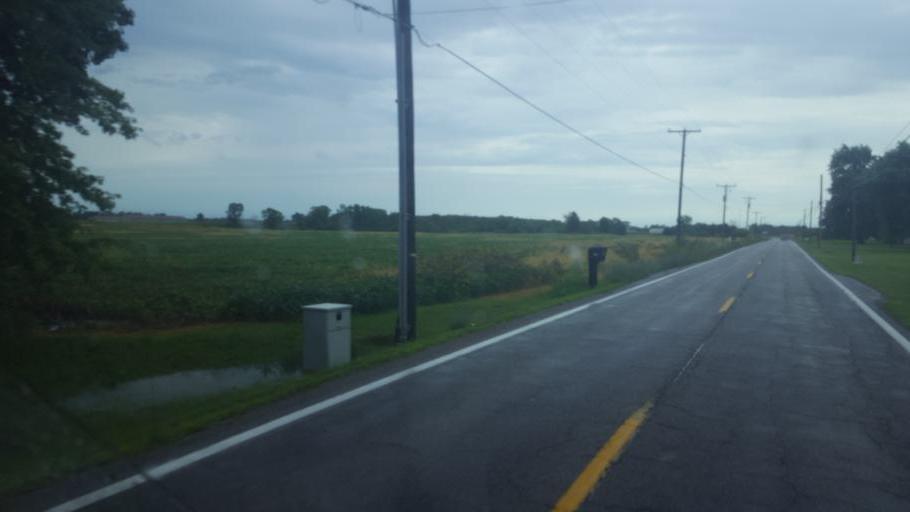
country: US
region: Ohio
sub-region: Marion County
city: Marion
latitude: 40.5531
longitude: -83.0803
